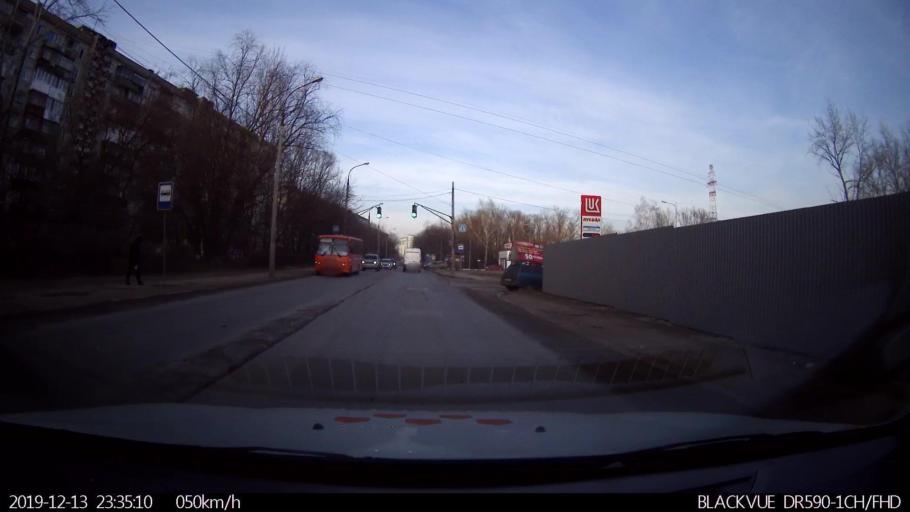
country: RU
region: Nizjnij Novgorod
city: Nizhniy Novgorod
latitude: 56.2874
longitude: 43.9533
